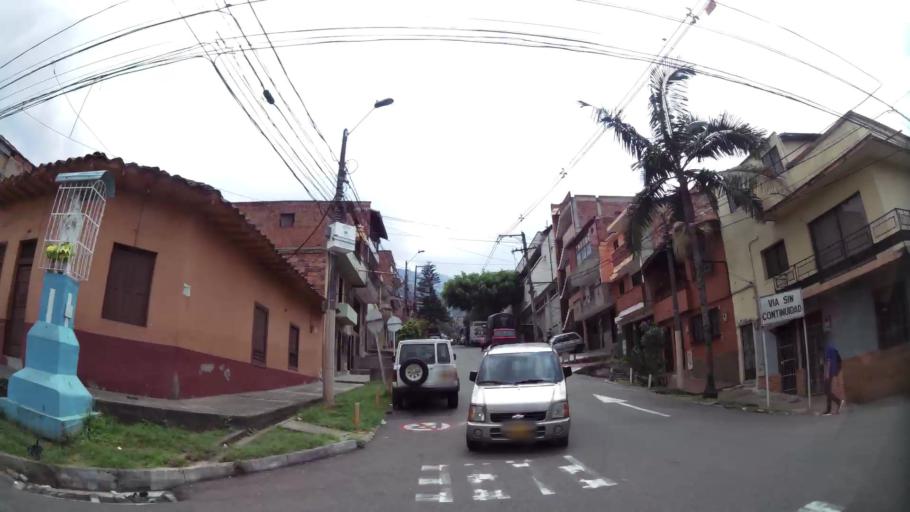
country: CO
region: Antioquia
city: Medellin
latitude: 6.2721
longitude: -75.5553
